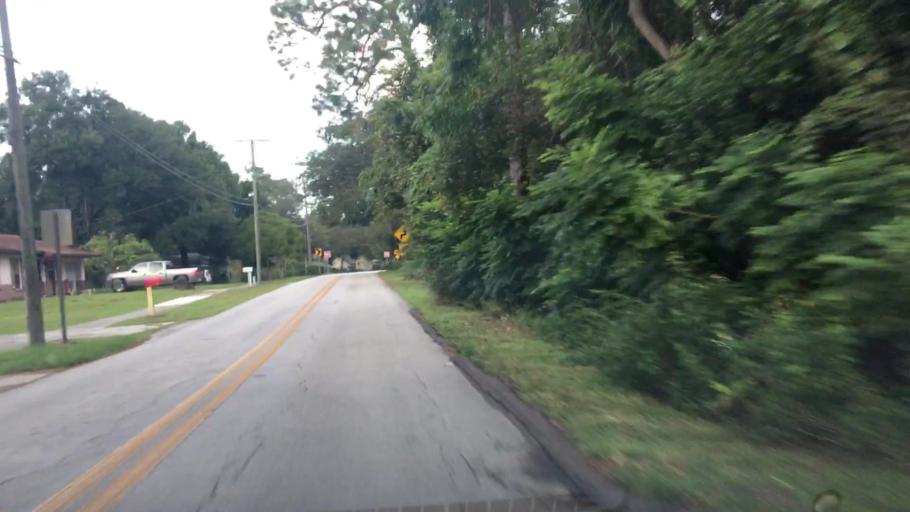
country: US
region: Florida
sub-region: Volusia County
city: DeBary
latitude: 28.8798
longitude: -81.3064
